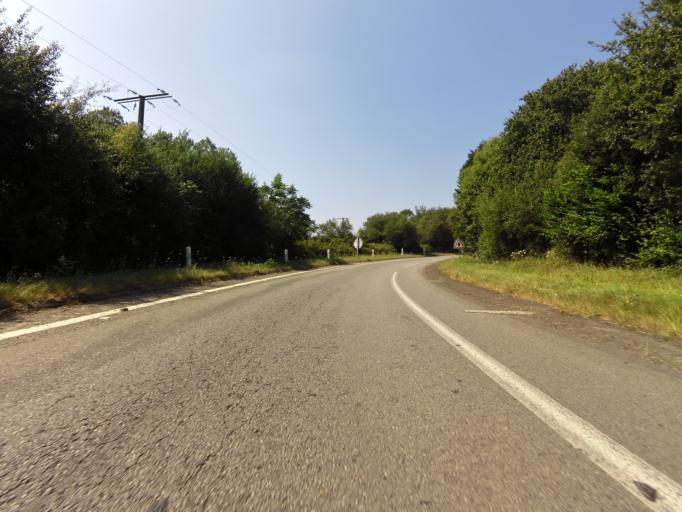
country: FR
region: Brittany
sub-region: Departement du Finistere
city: Pluguffan
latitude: 47.9533
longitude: -4.1780
